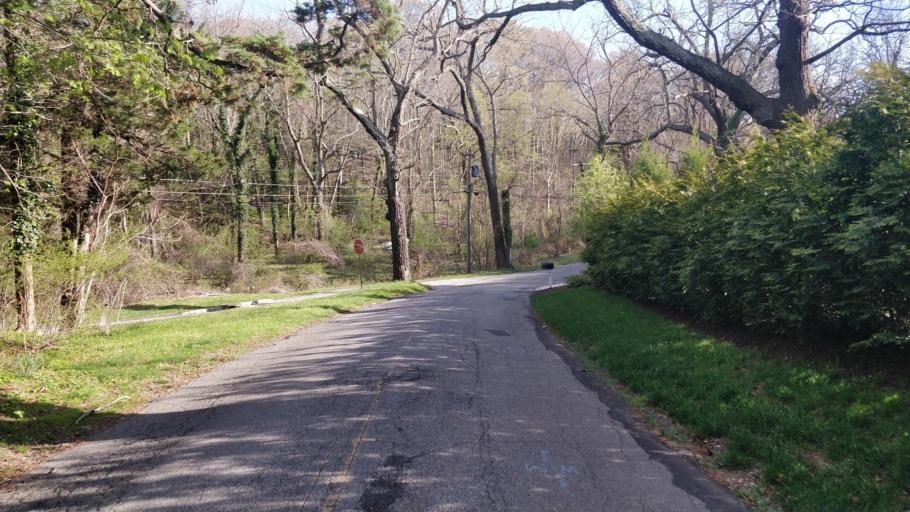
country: US
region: New York
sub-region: Suffolk County
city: Head of the Harbor
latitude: 40.8995
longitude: -73.1673
